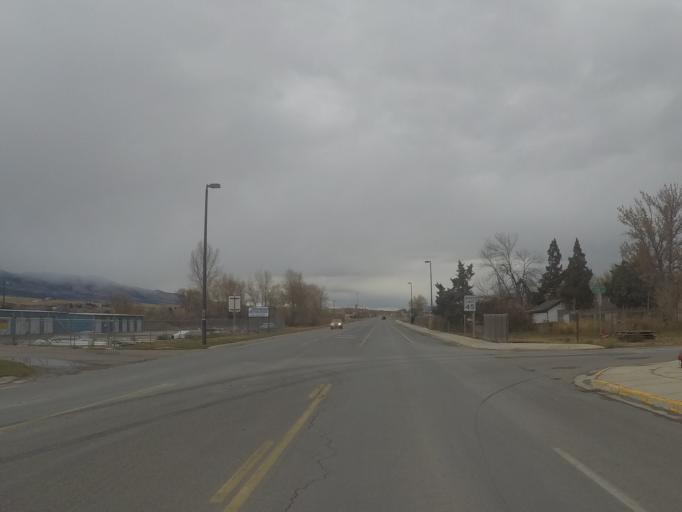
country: US
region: Montana
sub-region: Broadwater County
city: Townsend
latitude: 46.3247
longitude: -111.5251
